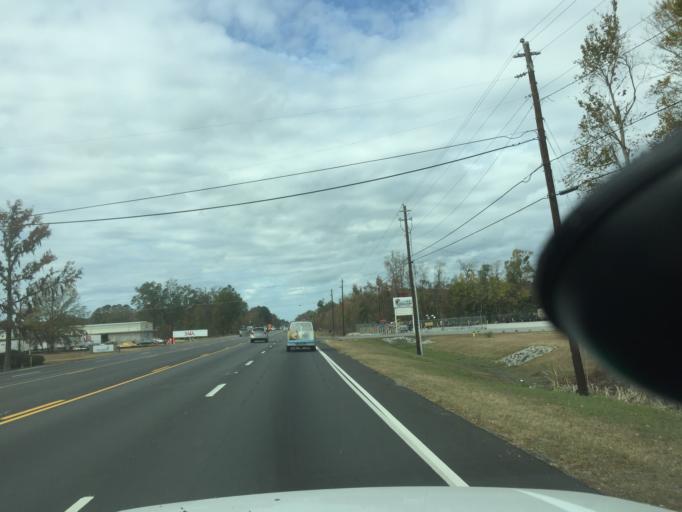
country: US
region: Georgia
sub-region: Chatham County
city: Garden City
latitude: 32.0897
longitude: -81.1831
